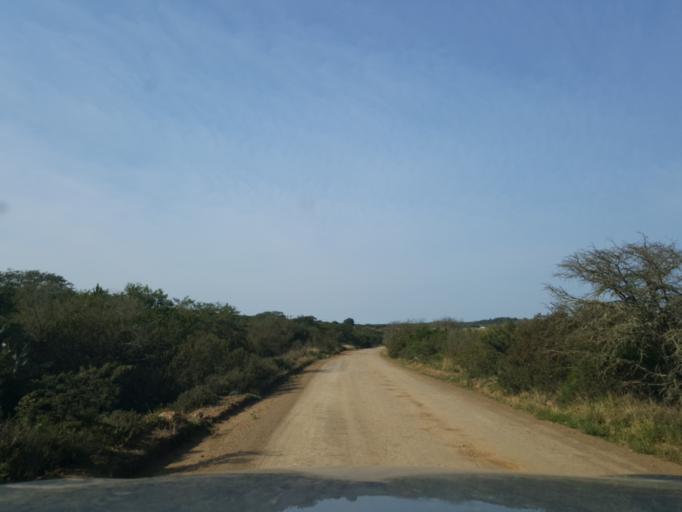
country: ZA
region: Eastern Cape
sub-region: Cacadu District Municipality
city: Grahamstown
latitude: -33.4041
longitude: 26.2950
